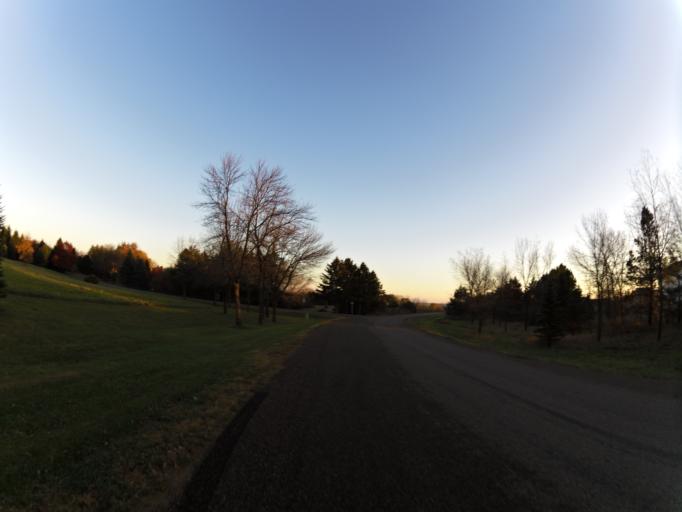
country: US
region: Minnesota
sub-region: Olmsted County
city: Rochester
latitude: 44.0486
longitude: -92.4087
